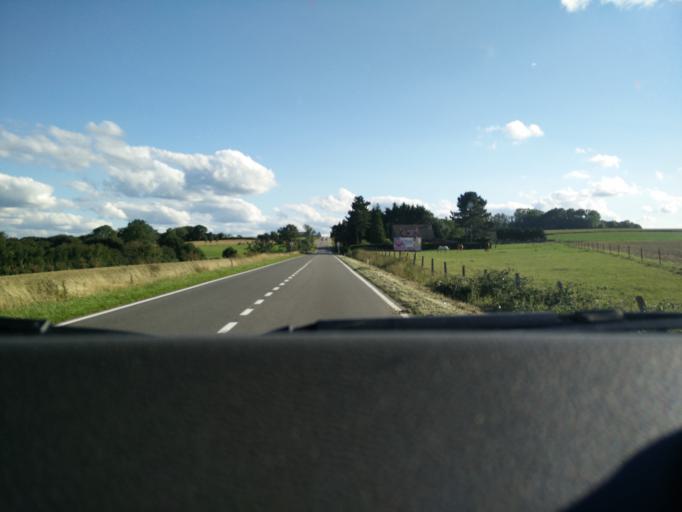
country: BE
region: Wallonia
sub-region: Province du Hainaut
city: Beaumont
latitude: 50.2080
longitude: 4.2254
